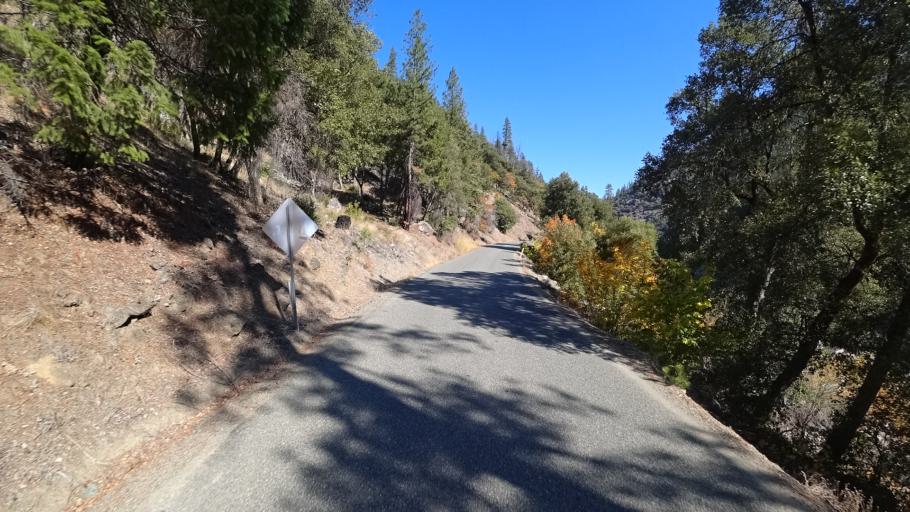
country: US
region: California
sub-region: Siskiyou County
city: Happy Camp
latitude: 41.6696
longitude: -123.1090
